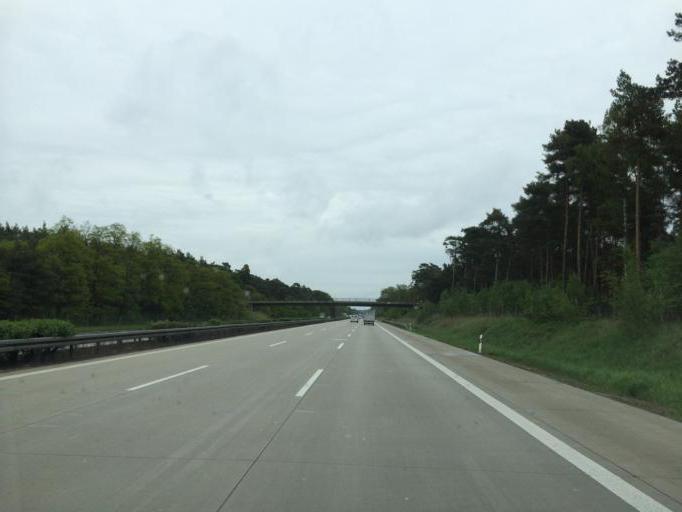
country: DE
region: Saxony-Anhalt
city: Burg bei Magdeburg
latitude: 52.2341
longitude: 11.9196
